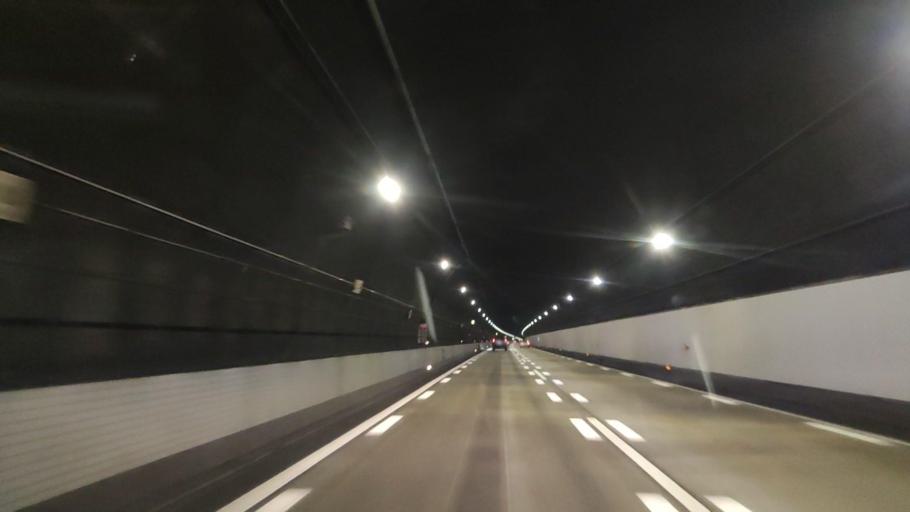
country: JP
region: Hiroshima
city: Fukuyama
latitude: 34.5019
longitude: 133.3246
